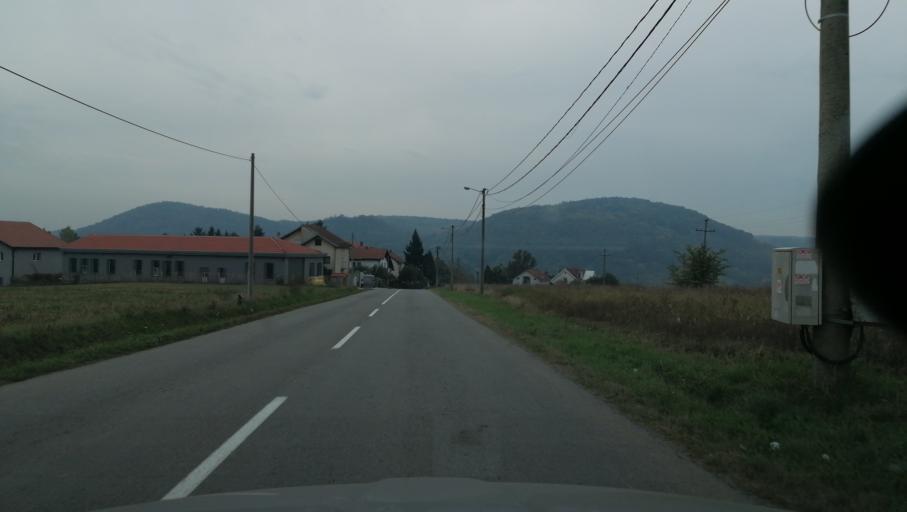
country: RS
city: Rusanj
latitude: 44.6724
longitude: 20.5029
